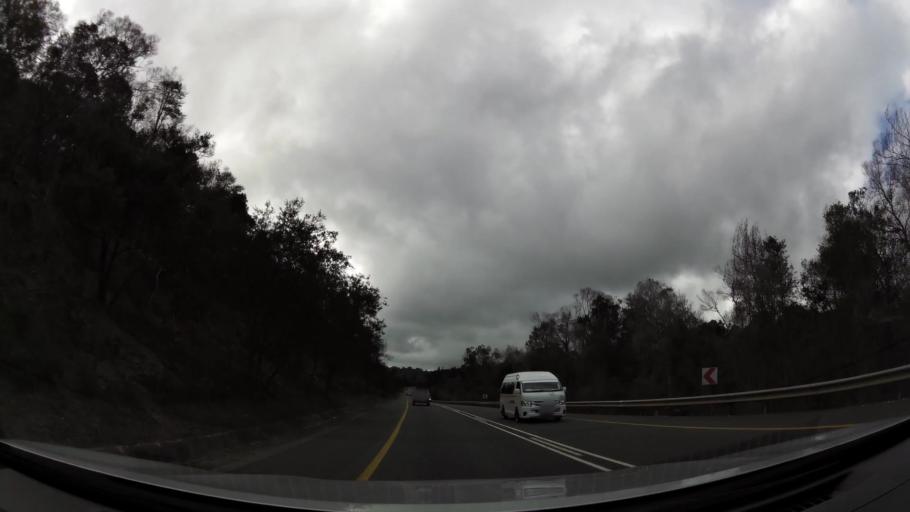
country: ZA
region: Western Cape
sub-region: Eden District Municipality
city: Knysna
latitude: -34.0334
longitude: 23.1586
